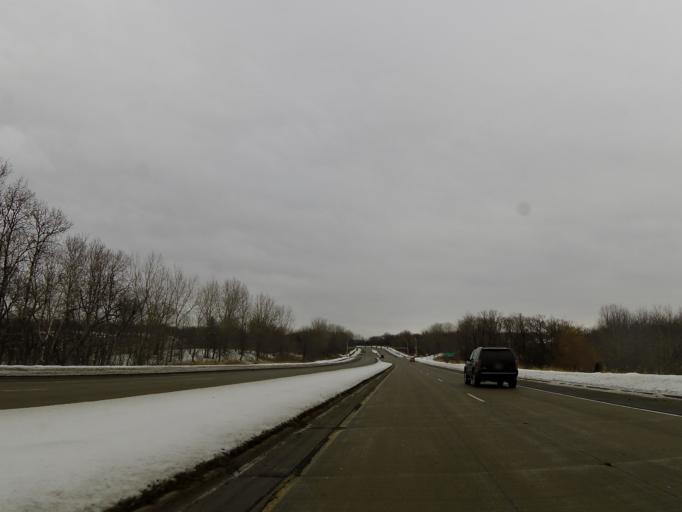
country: US
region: Minnesota
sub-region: Dakota County
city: Apple Valley
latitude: 44.7597
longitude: -93.2112
